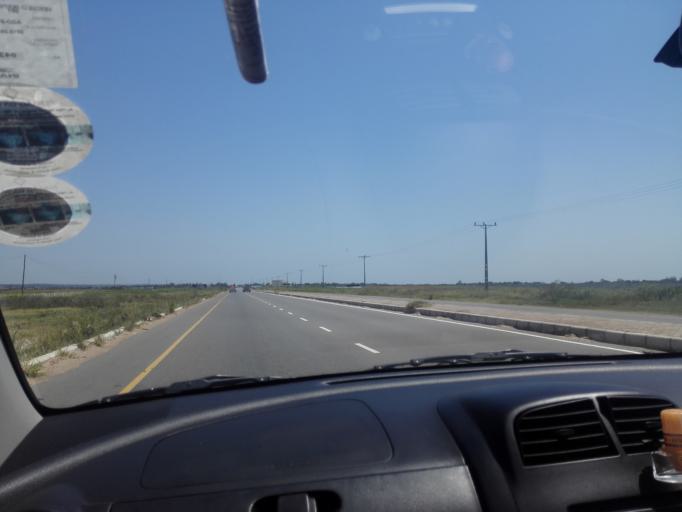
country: MZ
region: Maputo City
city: Maputo
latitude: -25.8340
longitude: 32.6727
